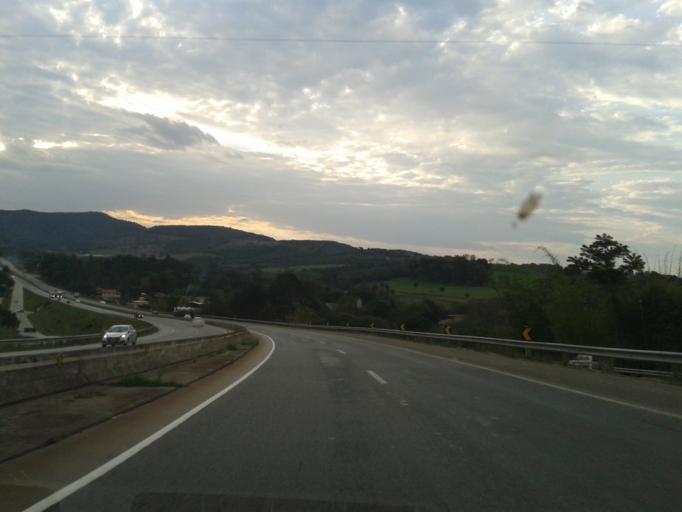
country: BR
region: Minas Gerais
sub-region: Juatuba
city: Juatuba
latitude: -19.9308
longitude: -44.3972
